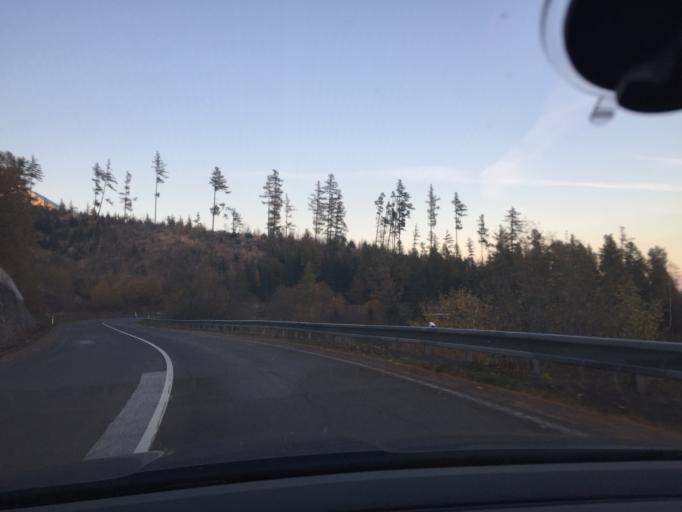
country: SK
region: Presovsky
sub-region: Okres Poprad
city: Strba
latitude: 49.1186
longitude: 20.1305
